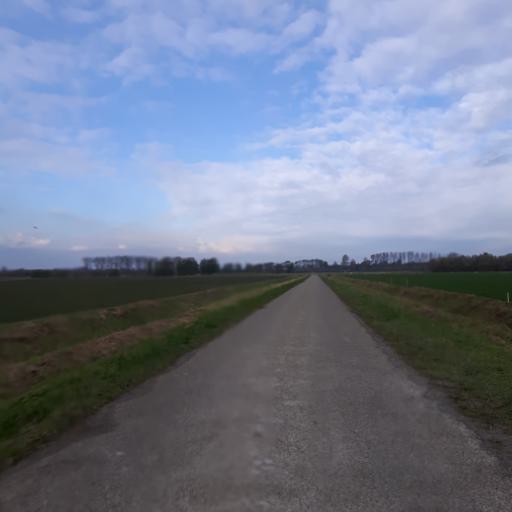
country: NL
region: Zeeland
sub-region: Gemeente Goes
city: Goes
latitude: 51.4910
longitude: 3.8392
